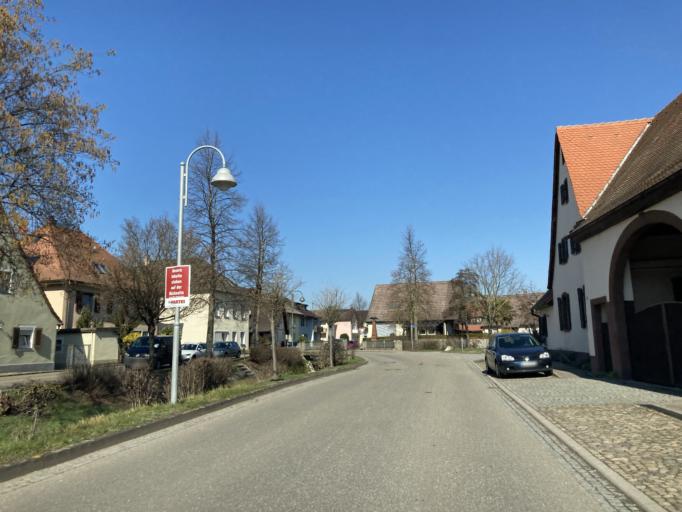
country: DE
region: Baden-Wuerttemberg
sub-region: Freiburg Region
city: Eschbach
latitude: 47.8898
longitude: 7.6518
